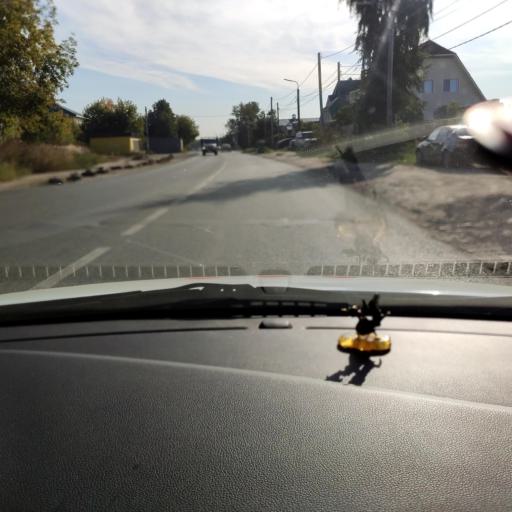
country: RU
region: Tatarstan
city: Staroye Arakchino
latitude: 55.8009
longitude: 49.0077
